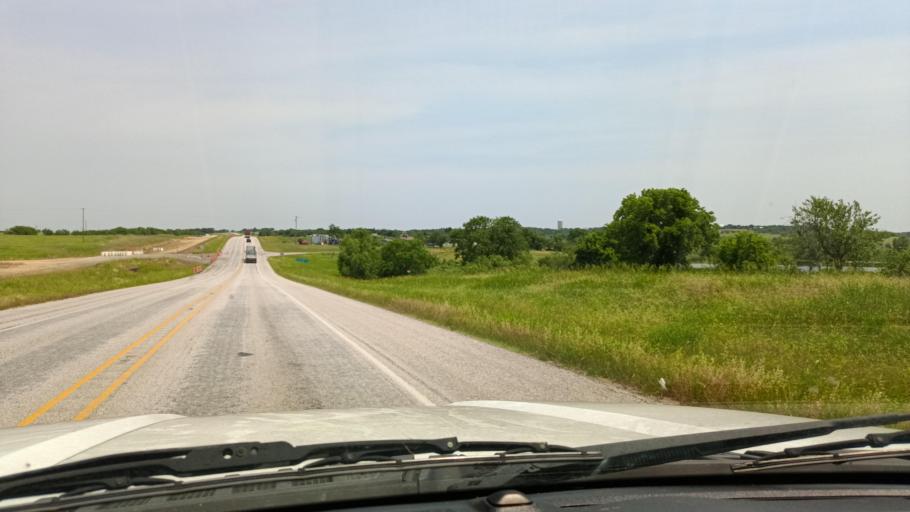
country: US
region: Texas
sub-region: Bell County
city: Rogers
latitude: 30.9678
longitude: -97.2659
